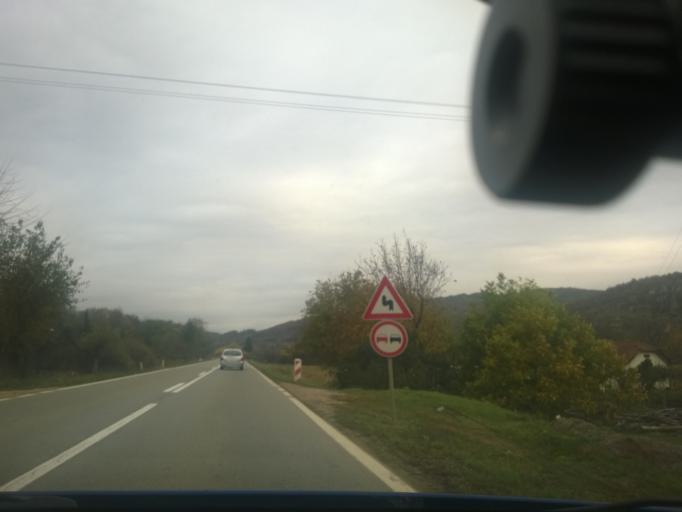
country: RS
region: Central Serbia
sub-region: Pirotski Okrug
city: Dimitrovgrad
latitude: 43.0304
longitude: 22.7203
